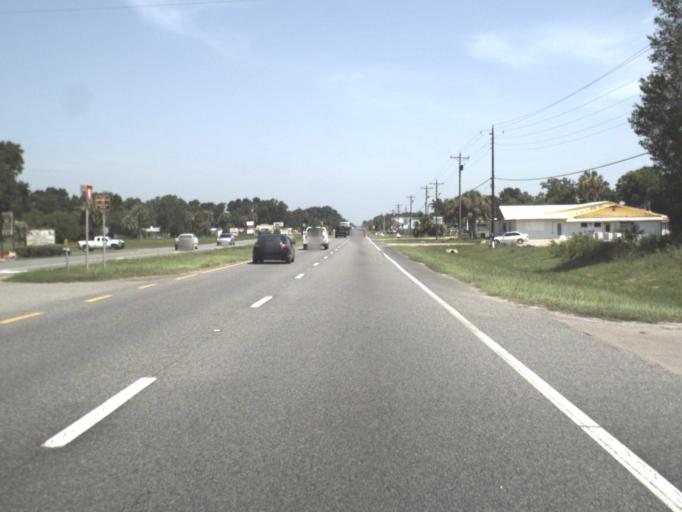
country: US
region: Florida
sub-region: Levy County
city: Chiefland
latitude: 29.5103
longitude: -82.8753
